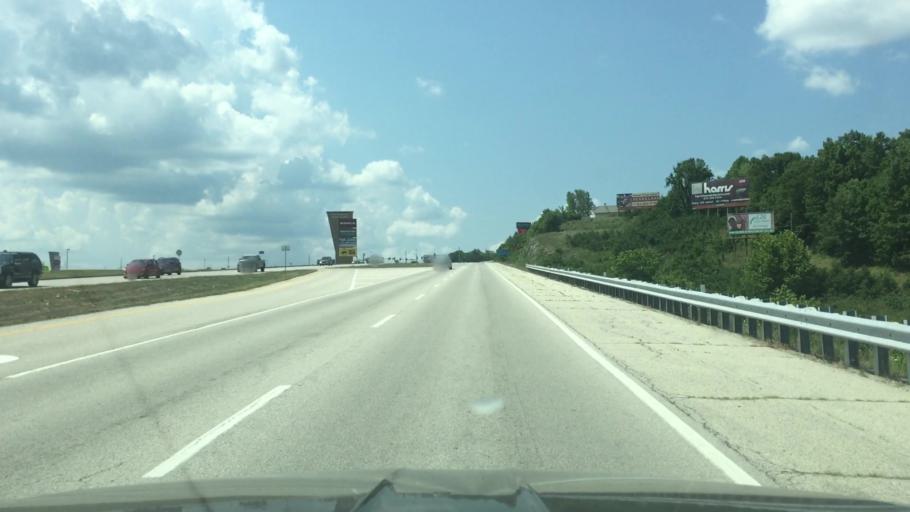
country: US
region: Missouri
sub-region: Miller County
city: Lake Ozark
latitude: 38.1795
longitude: -92.6130
